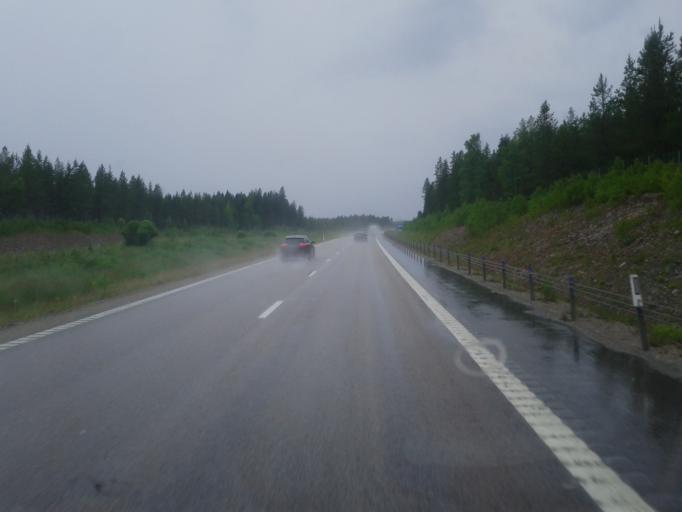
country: SE
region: Uppsala
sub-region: Tierps Kommun
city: Tierp
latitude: 60.4262
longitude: 17.4345
